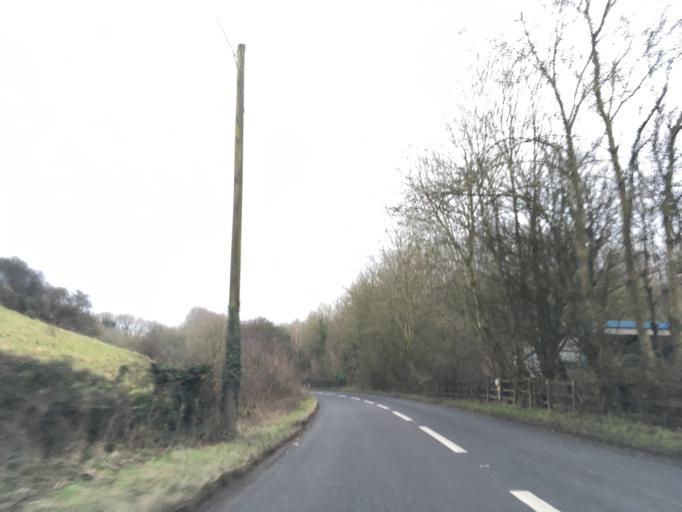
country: GB
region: England
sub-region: South Gloucestershire
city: Hinton
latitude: 51.5014
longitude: -2.3656
